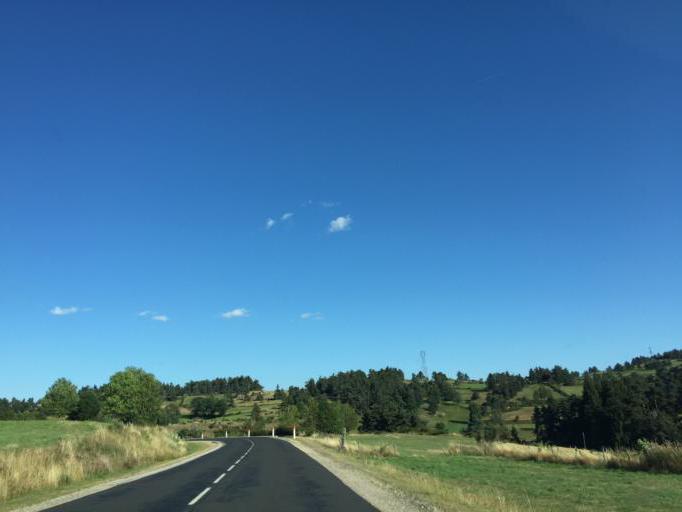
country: FR
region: Auvergne
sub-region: Departement de la Haute-Loire
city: Saugues
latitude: 44.9641
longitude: 3.6024
